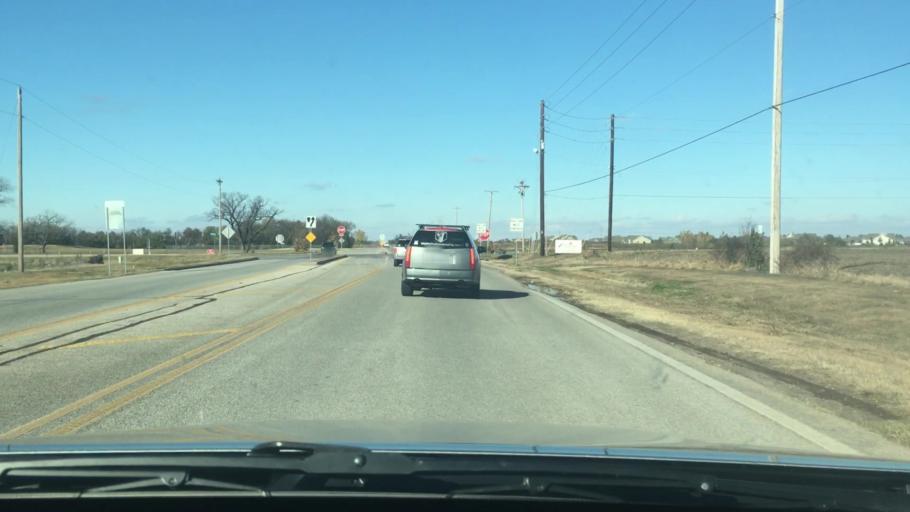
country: US
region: Kansas
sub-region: Sedgwick County
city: Maize
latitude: 37.7359
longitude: -97.4810
